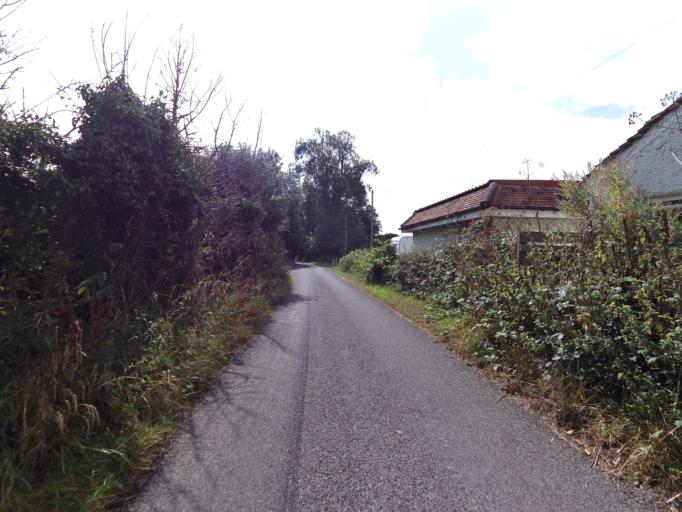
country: GB
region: England
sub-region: Hertfordshire
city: Shenley AV
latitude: 51.6975
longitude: -0.2551
